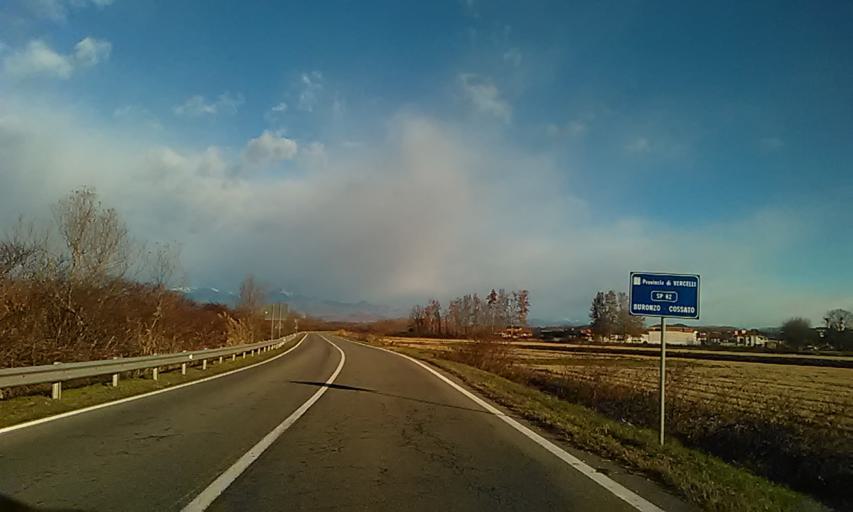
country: IT
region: Piedmont
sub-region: Provincia di Vercelli
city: Buronzo
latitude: 45.4716
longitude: 8.2604
